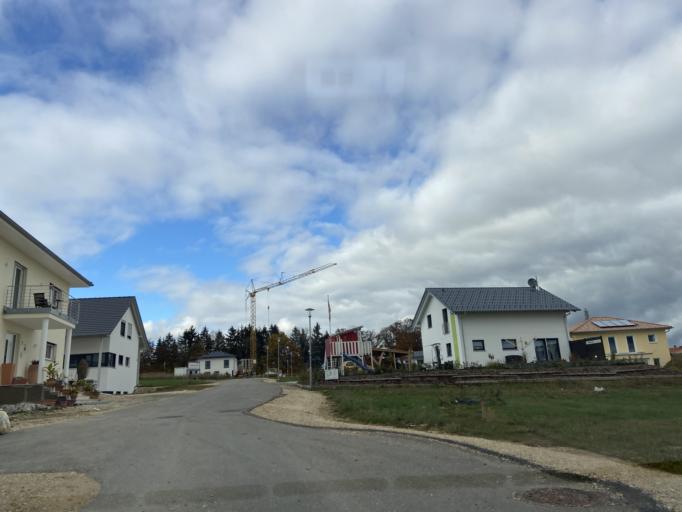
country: DE
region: Baden-Wuerttemberg
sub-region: Tuebingen Region
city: Inzigkofen
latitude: 48.0688
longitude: 9.1687
